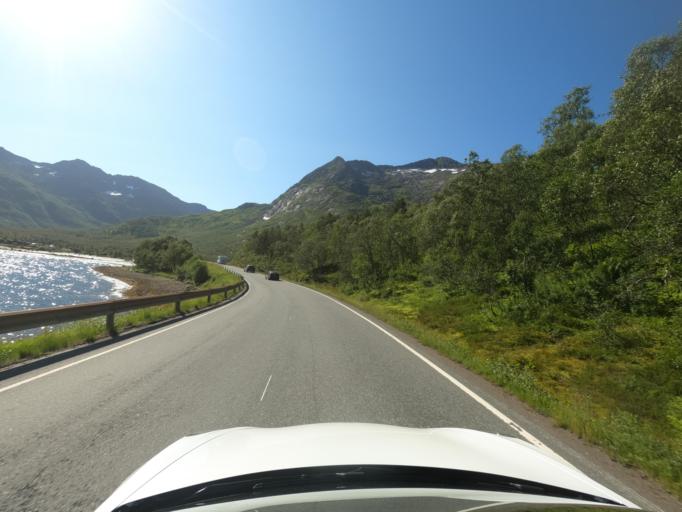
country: NO
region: Nordland
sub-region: Lodingen
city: Lodingen
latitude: 68.5369
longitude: 15.7222
